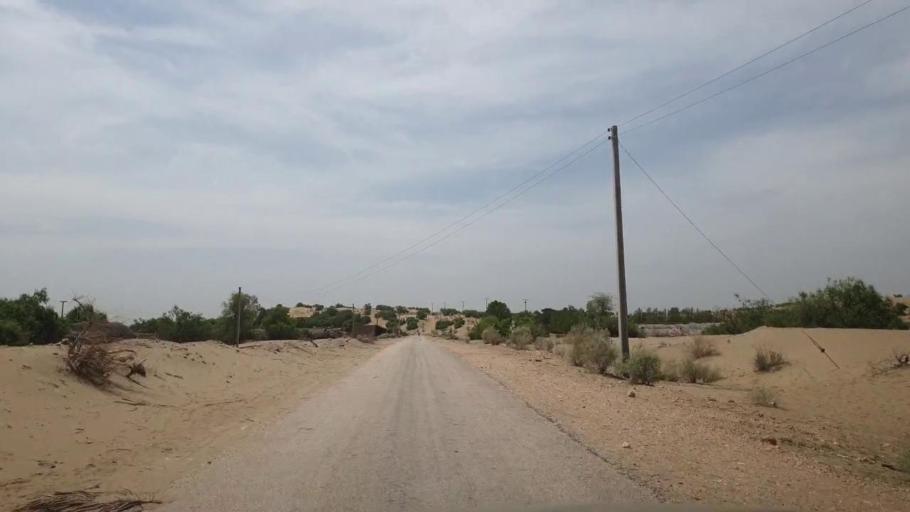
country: PK
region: Sindh
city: Kot Diji
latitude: 27.1083
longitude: 69.0769
